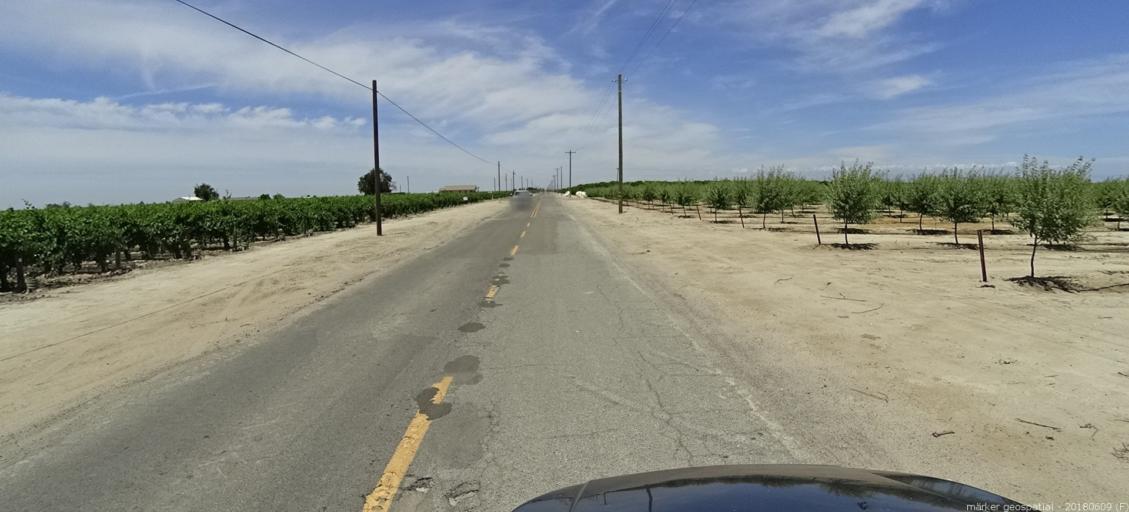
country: US
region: California
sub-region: Madera County
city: Parkwood
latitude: 36.8573
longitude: -120.0922
